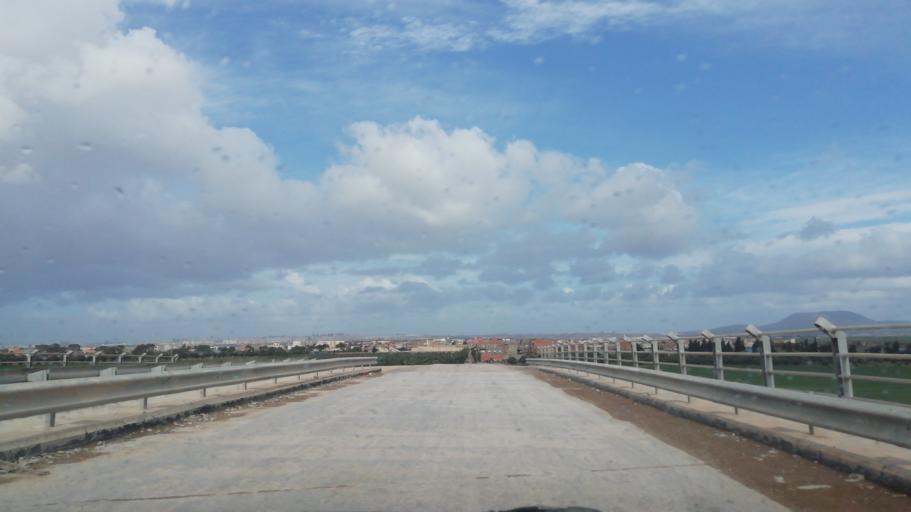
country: DZ
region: Oran
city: Sidi ech Chahmi
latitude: 35.6481
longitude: -0.5177
